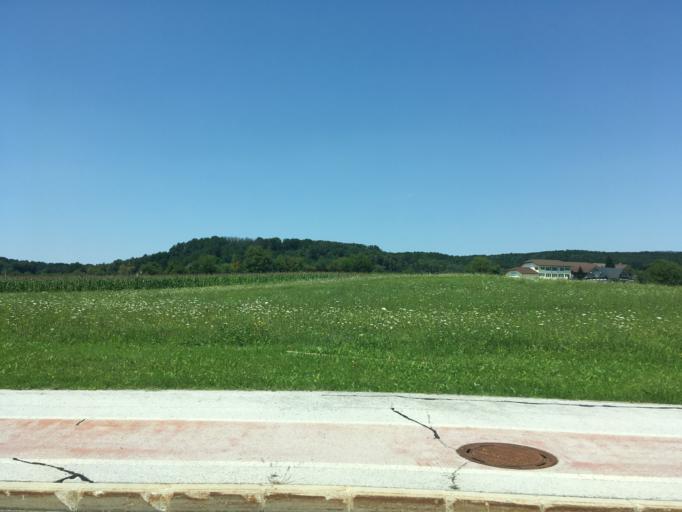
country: SI
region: Metlika
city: Metlika
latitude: 45.6508
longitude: 15.3037
